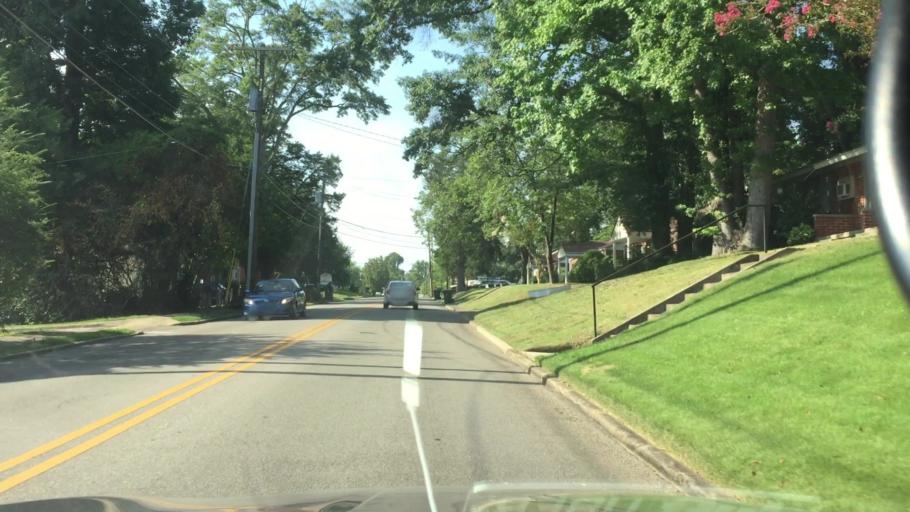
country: US
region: Alabama
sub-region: Lee County
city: Auburn
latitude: 32.6048
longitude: -85.4748
